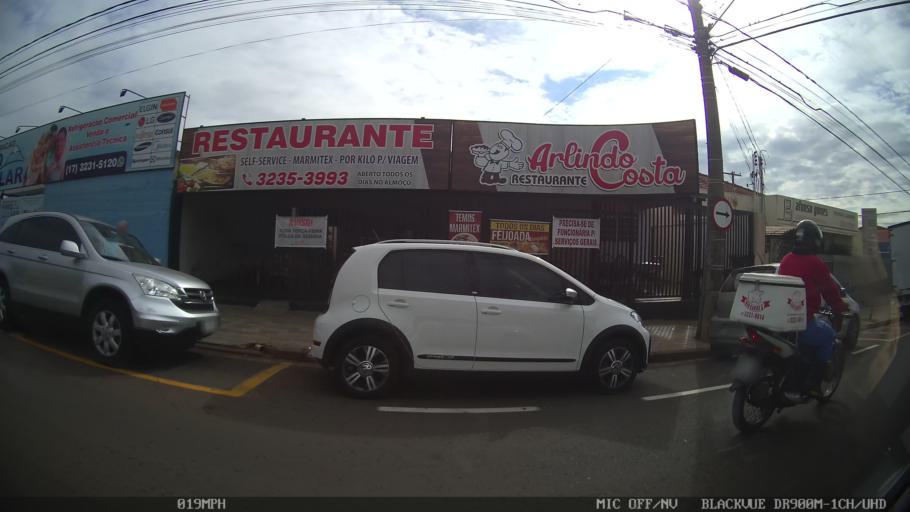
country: BR
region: Sao Paulo
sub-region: Sao Jose Do Rio Preto
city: Sao Jose do Rio Preto
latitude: -20.8167
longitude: -49.3700
